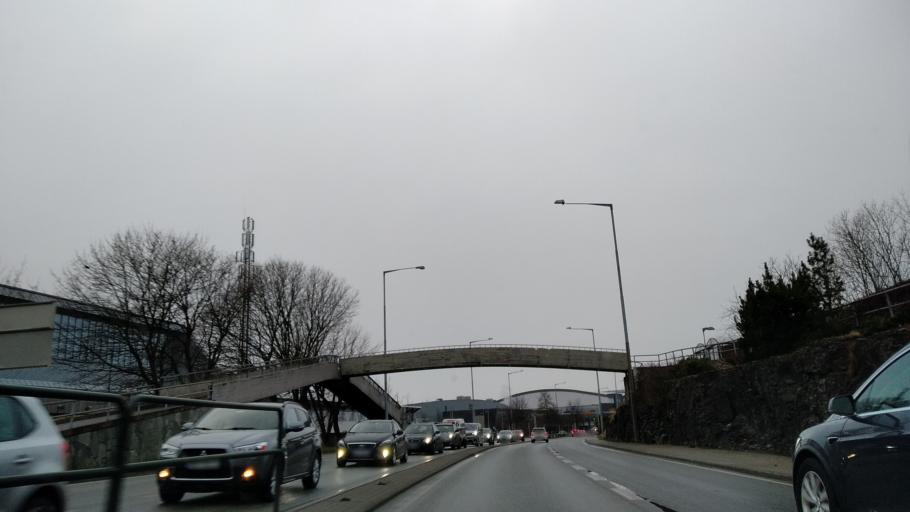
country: NO
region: Rogaland
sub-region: Stavanger
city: Stavanger
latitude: 58.9554
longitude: 5.6967
